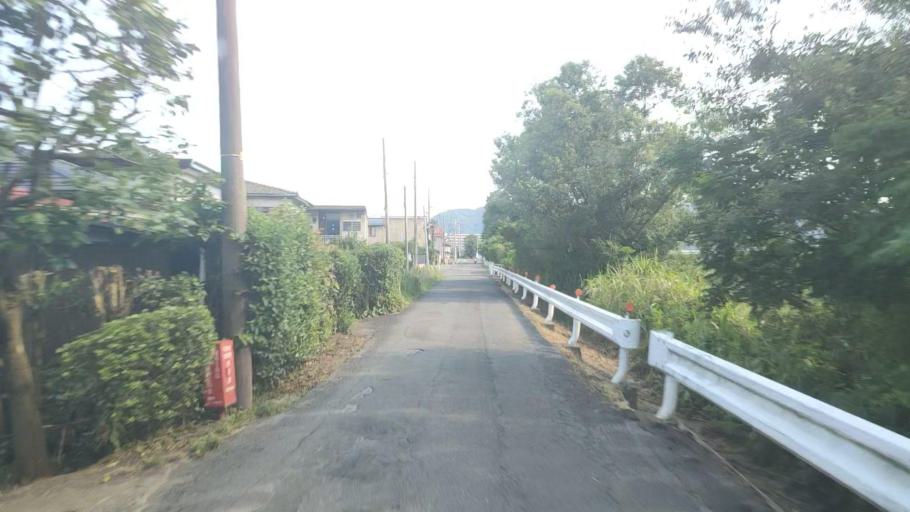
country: JP
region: Kanagawa
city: Hiratsuka
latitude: 35.3420
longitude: 139.3232
